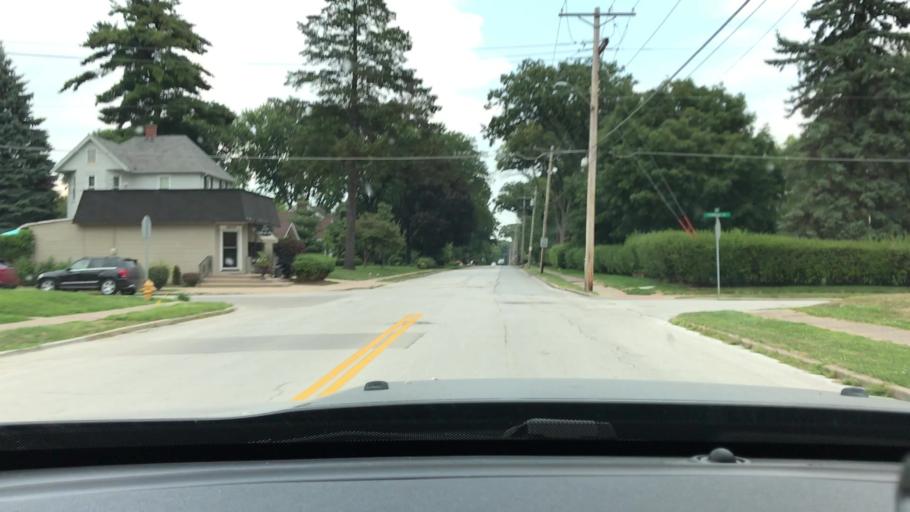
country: US
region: Iowa
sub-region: Scott County
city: Bettendorf
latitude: 41.5365
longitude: -90.5326
